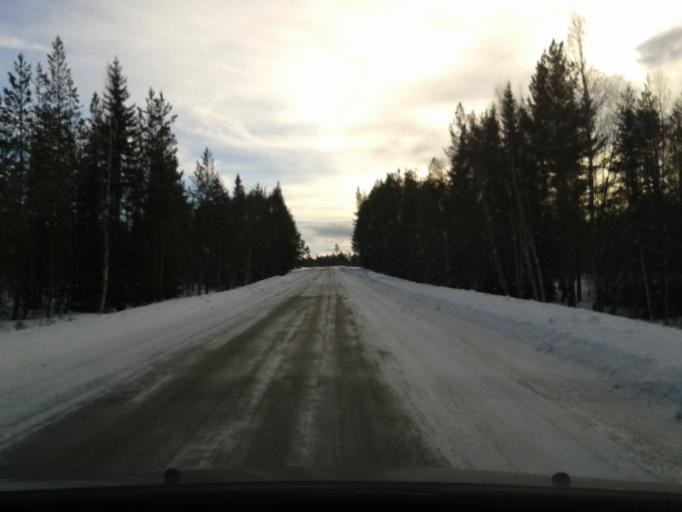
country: SE
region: Vaesterbotten
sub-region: Asele Kommun
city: Asele
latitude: 64.2404
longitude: 17.2948
